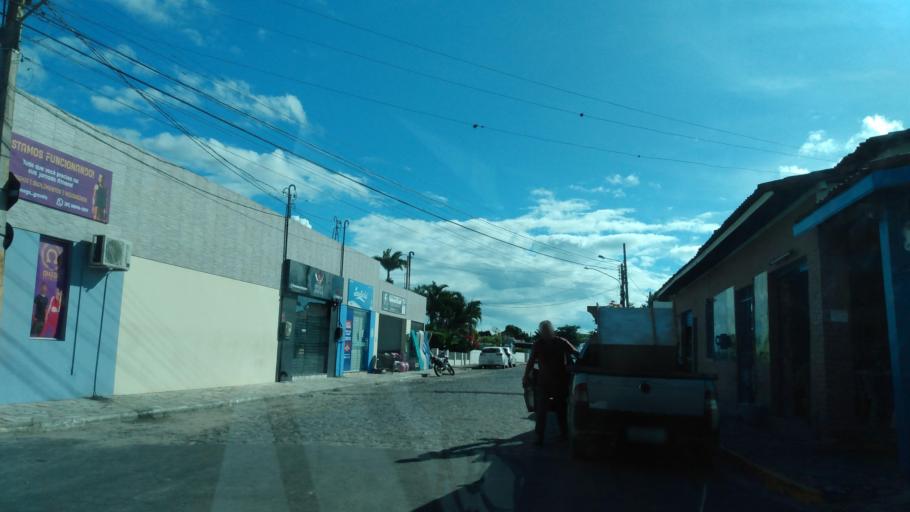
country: ET
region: Oromiya
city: Gore
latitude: 8.1956
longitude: 35.5611
